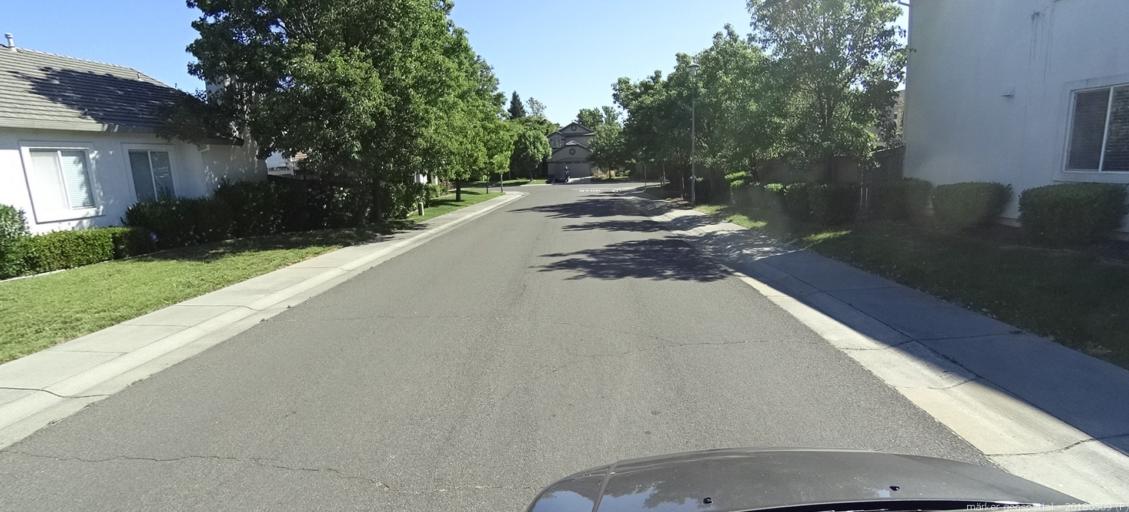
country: US
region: California
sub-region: Sacramento County
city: Elverta
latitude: 38.6692
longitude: -121.5216
